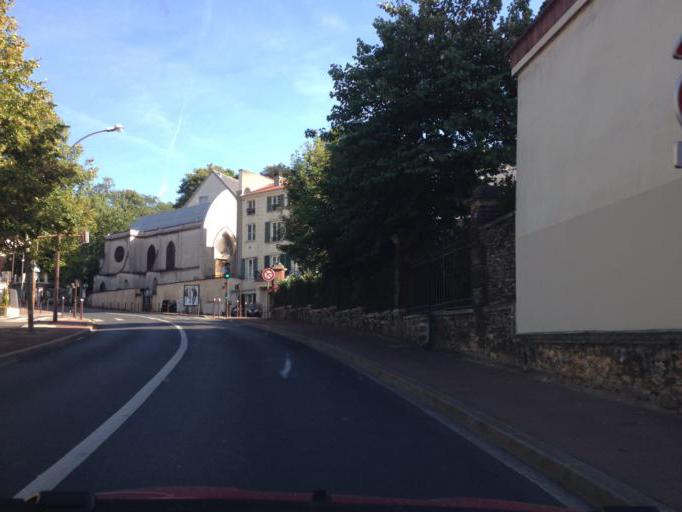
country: FR
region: Ile-de-France
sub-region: Departement des Hauts-de-Seine
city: Sevres
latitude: 48.8239
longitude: 2.2203
